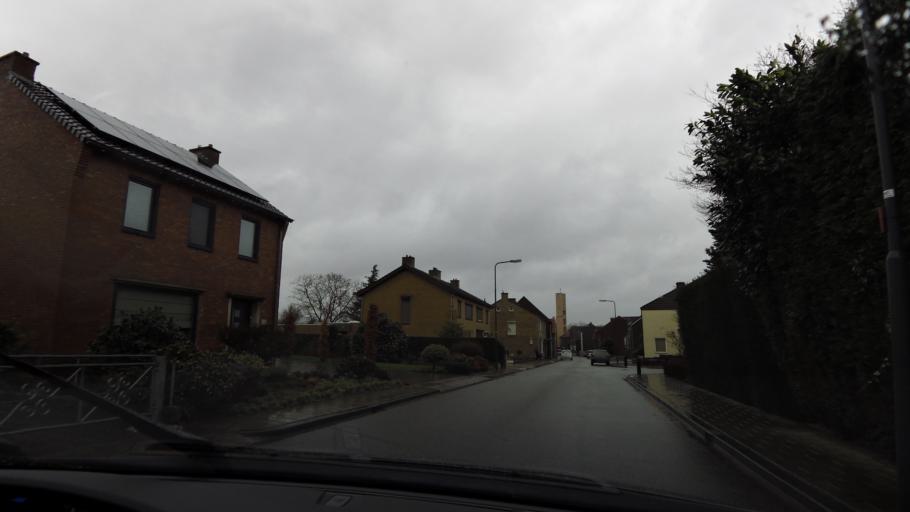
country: NL
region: Limburg
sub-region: Gemeente Sittard-Geleen
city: Born
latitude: 51.0116
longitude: 5.8158
